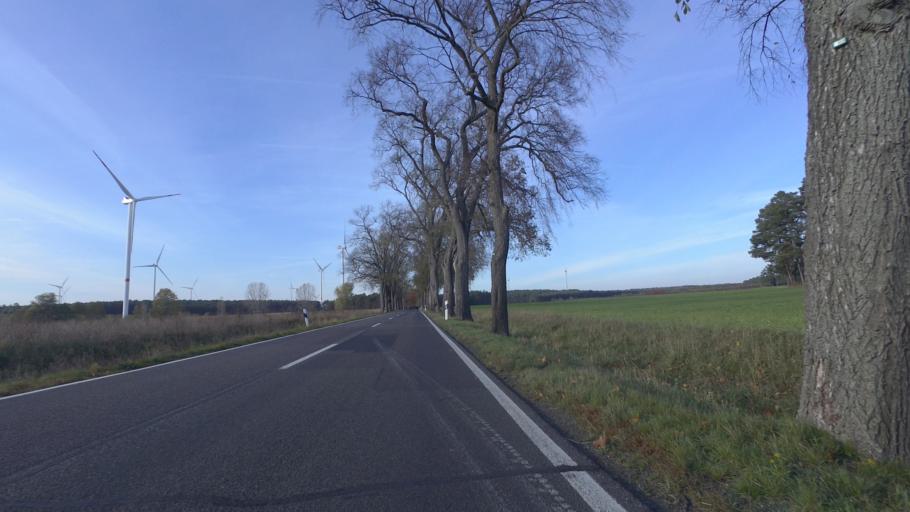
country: DE
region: Brandenburg
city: Sperenberg
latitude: 52.1958
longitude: 13.3154
